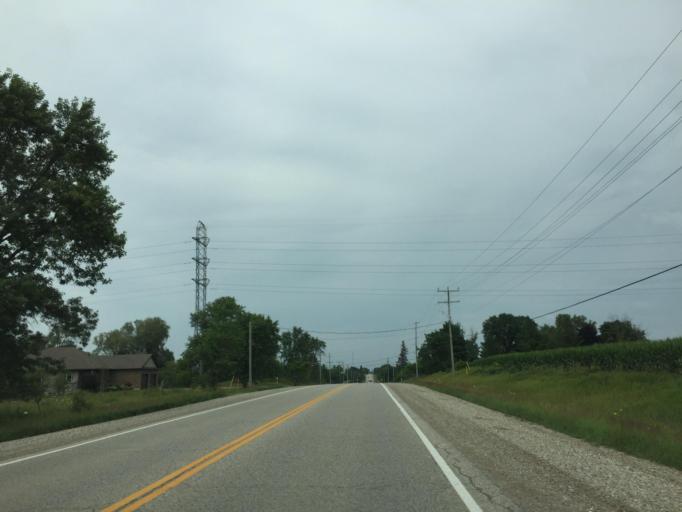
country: CA
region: Ontario
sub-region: Wellington County
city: Guelph
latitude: 43.5754
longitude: -80.3138
